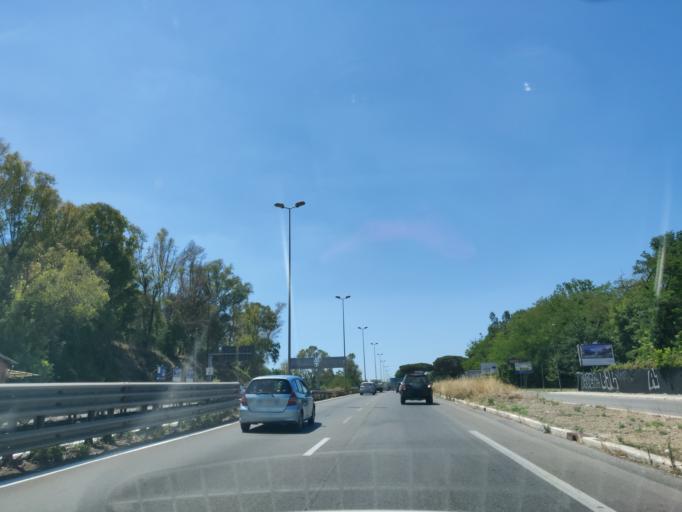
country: IT
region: Latium
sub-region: Citta metropolitana di Roma Capitale
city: Selcetta
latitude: 41.8139
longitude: 12.4605
